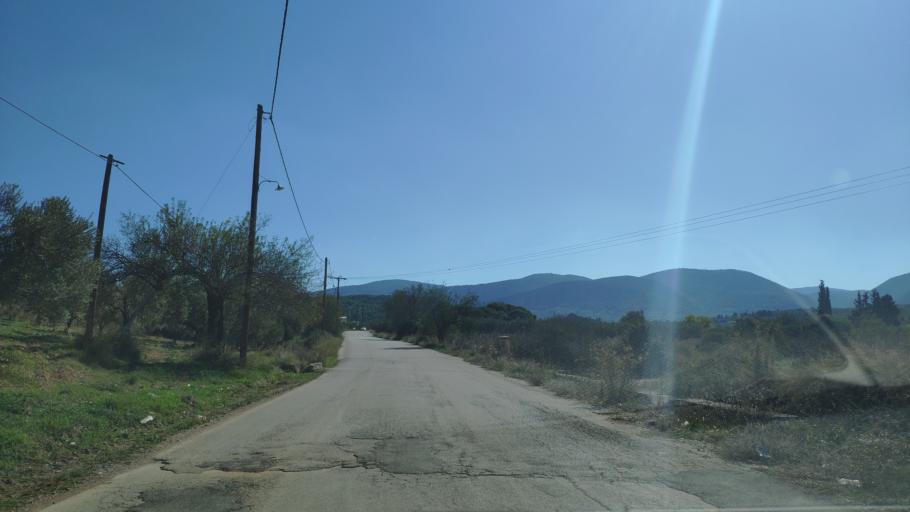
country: GR
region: Peloponnese
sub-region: Nomos Korinthias
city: Athikia
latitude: 37.8400
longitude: 22.9097
